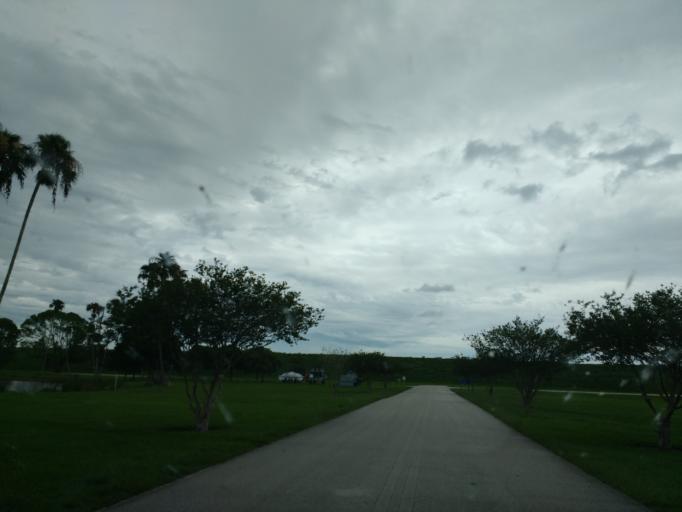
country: US
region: Florida
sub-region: Palm Beach County
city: South Bay
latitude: 26.6968
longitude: -80.8105
